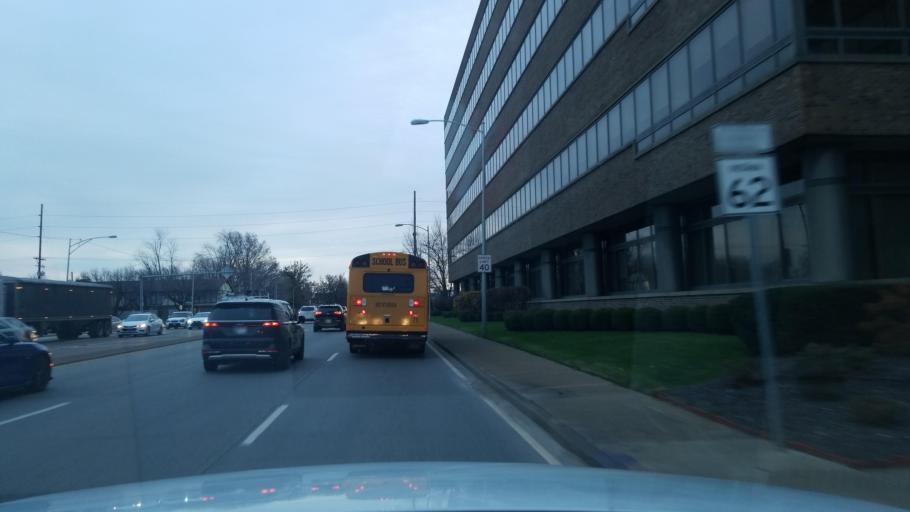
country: US
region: Indiana
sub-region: Vanderburgh County
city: Evansville
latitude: 37.9778
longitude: -87.6003
